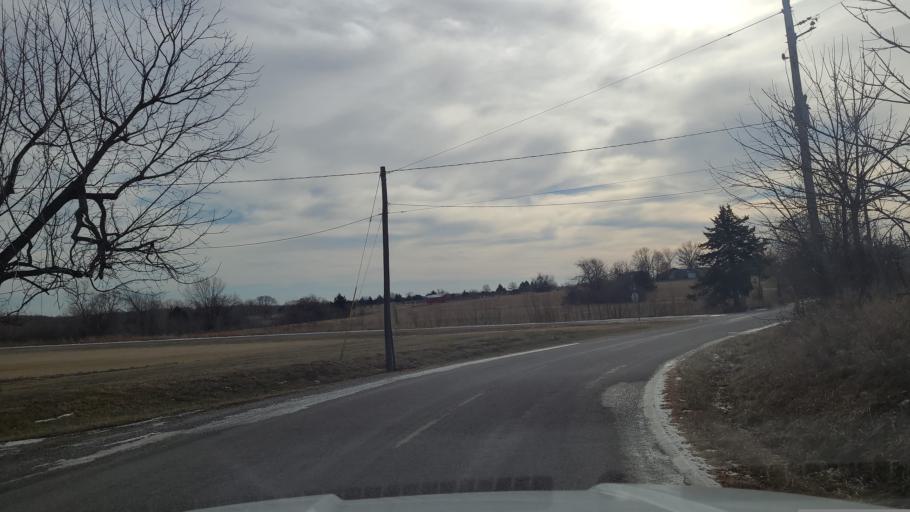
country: US
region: Kansas
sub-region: Douglas County
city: Lawrence
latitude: 38.9106
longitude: -95.2146
